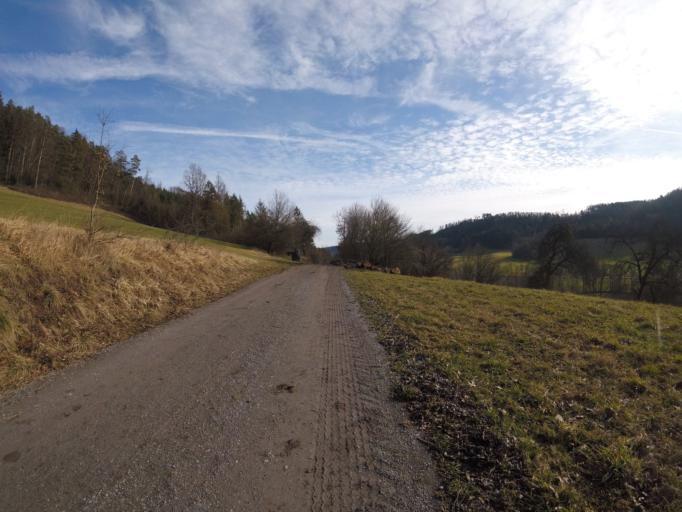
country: DE
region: Baden-Wuerttemberg
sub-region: Regierungsbezirk Stuttgart
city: Kaisersbach
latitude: 48.9754
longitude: 9.6217
